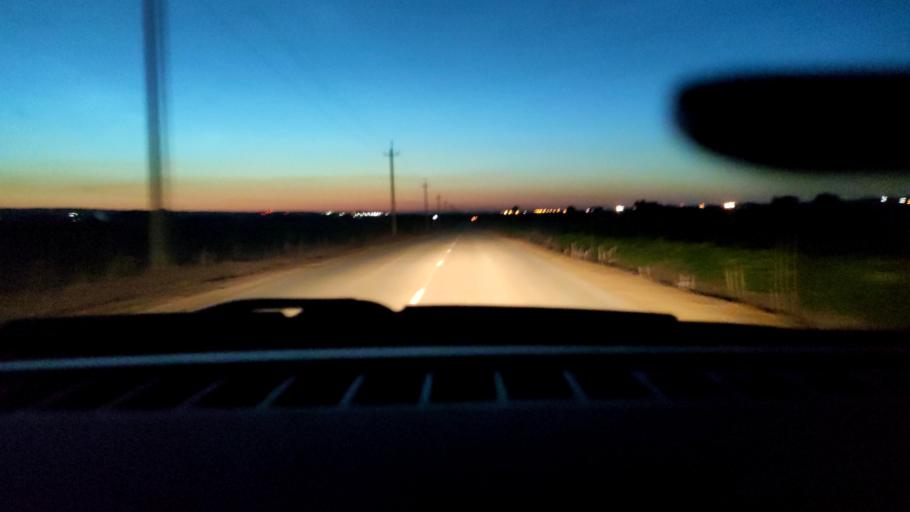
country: RU
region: Perm
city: Kultayevo
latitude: 57.8893
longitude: 55.9902
